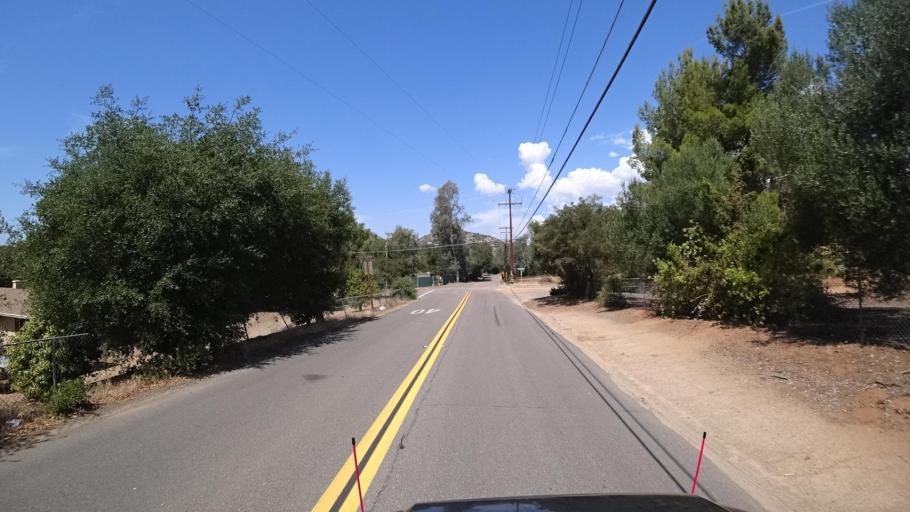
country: US
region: California
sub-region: San Diego County
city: Valley Center
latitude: 33.2421
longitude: -116.9933
